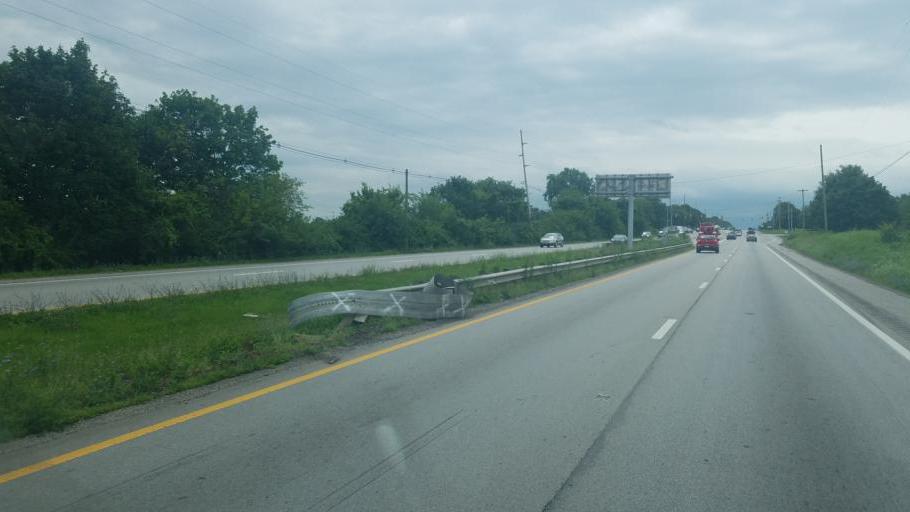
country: US
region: Ohio
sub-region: Franklin County
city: Obetz
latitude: 39.8654
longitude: -83.0049
